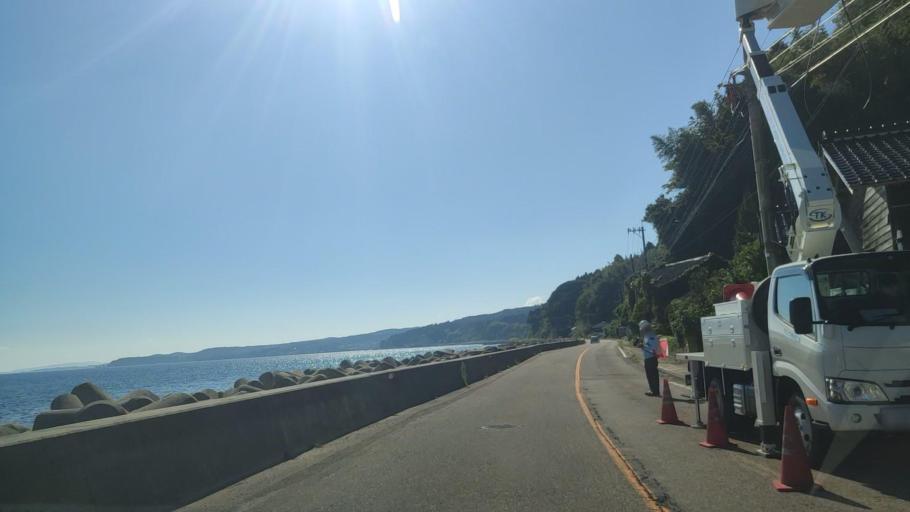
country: JP
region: Ishikawa
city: Nanao
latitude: 37.2907
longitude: 137.1269
